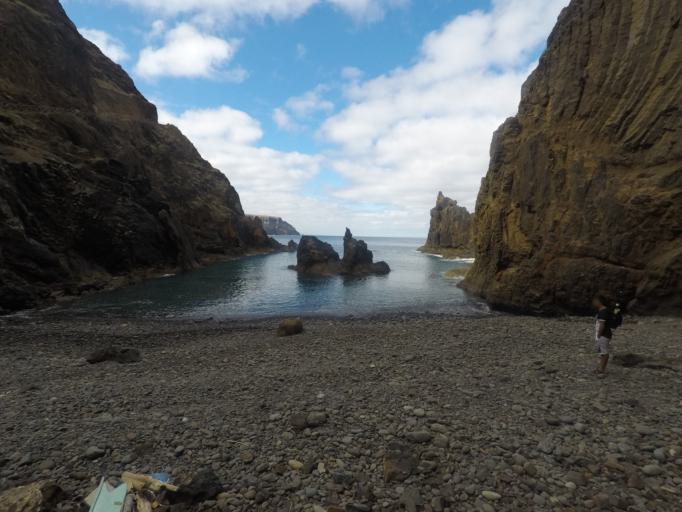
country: PT
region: Madeira
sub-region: Porto Santo
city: Vila de Porto Santo
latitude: 33.0329
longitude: -16.3874
